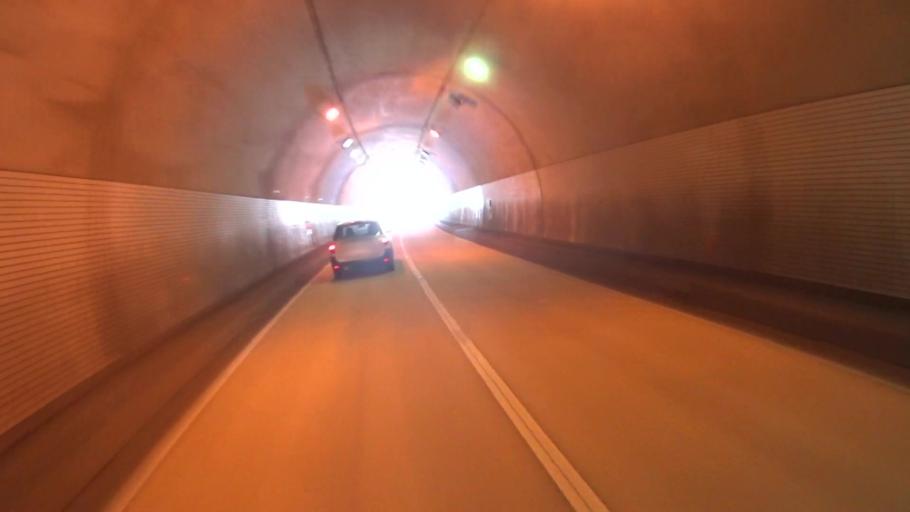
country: JP
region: Kyoto
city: Kameoka
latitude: 35.1060
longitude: 135.5568
